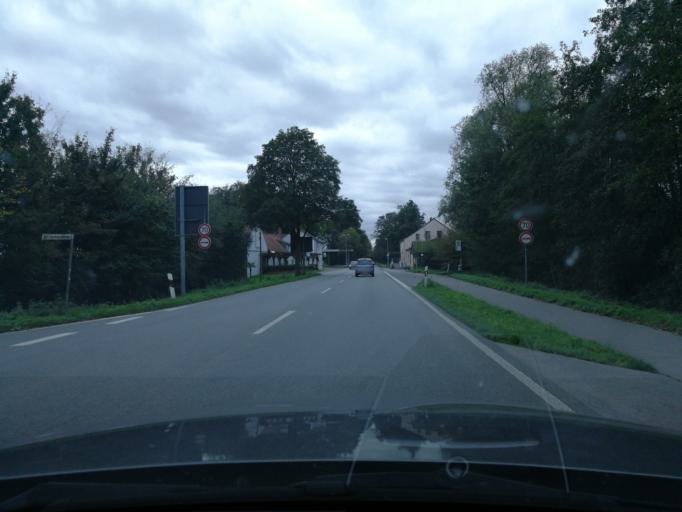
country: NL
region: Limburg
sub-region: Gemeente Venlo
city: Venlo
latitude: 51.4058
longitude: 6.2174
